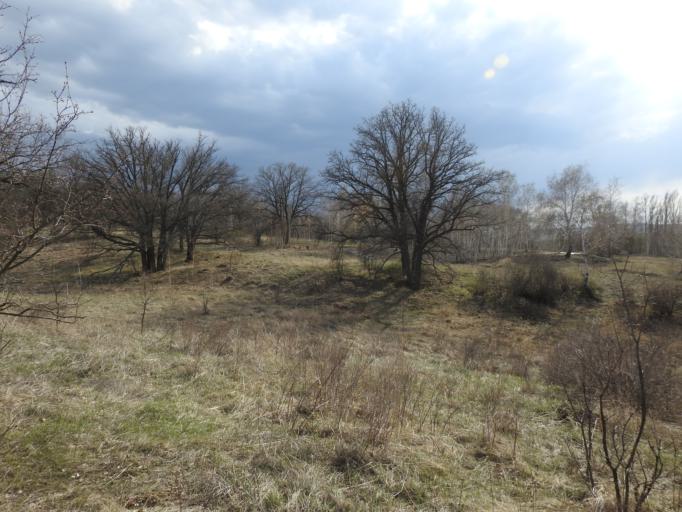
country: RU
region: Saratov
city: Krasnyy Oktyabr'
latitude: 51.4241
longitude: 45.5437
